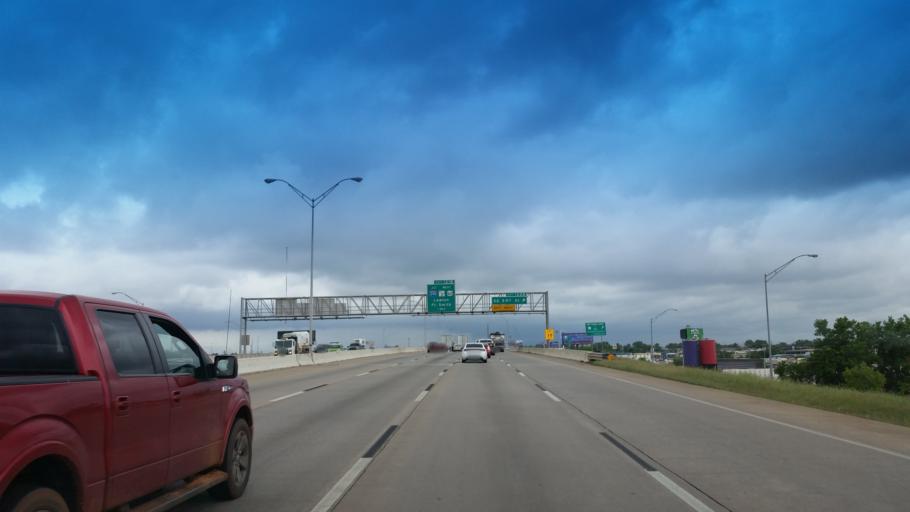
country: US
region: Oklahoma
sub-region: Oklahoma County
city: Del City
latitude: 35.4108
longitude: -97.4924
